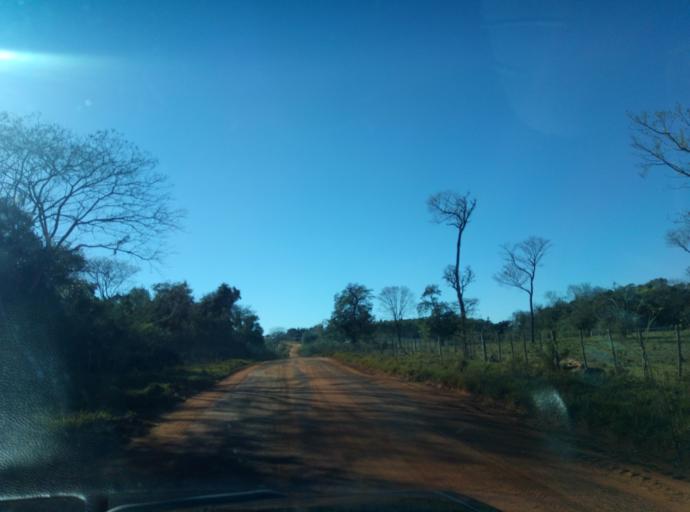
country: PY
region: Caaguazu
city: Doctor Cecilio Baez
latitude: -25.1637
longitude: -56.2573
